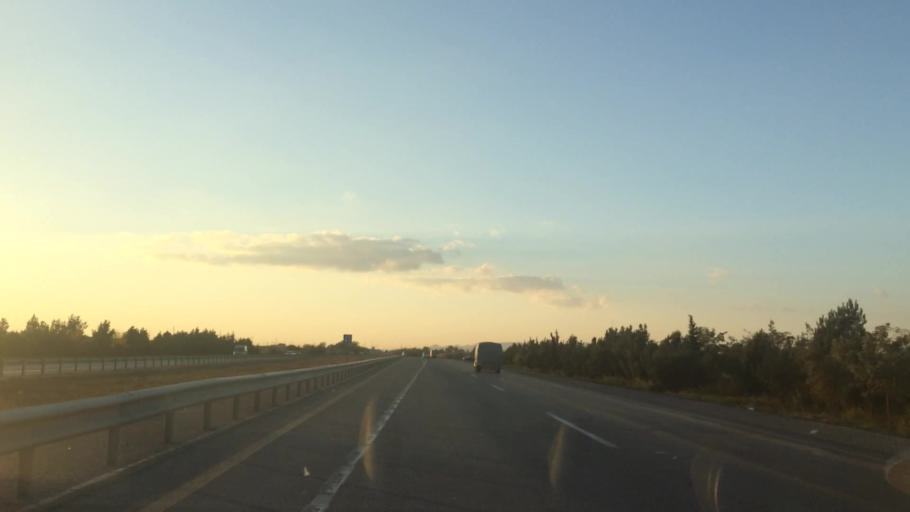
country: AZ
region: Haciqabul
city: Haciqabul
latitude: 40.0250
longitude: 49.1132
